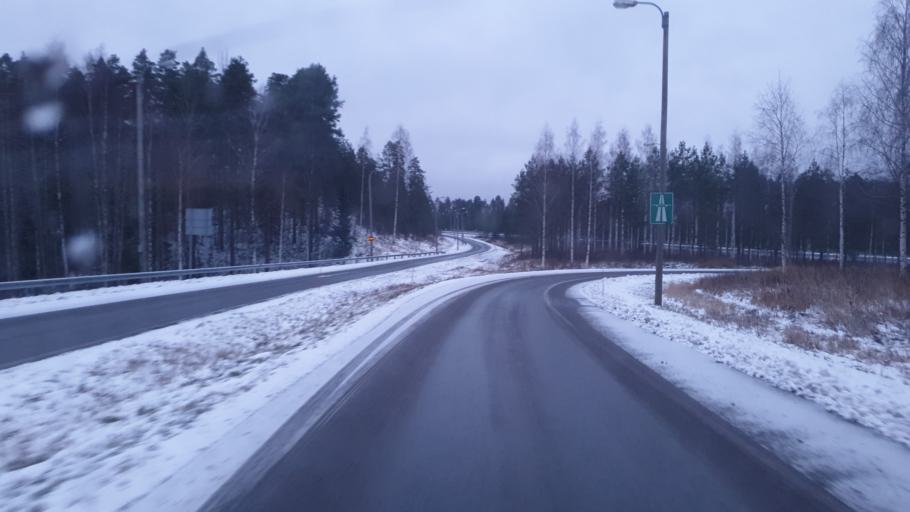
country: FI
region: Northern Savo
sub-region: Kuopio
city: Siilinjaervi
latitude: 63.0598
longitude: 27.6685
